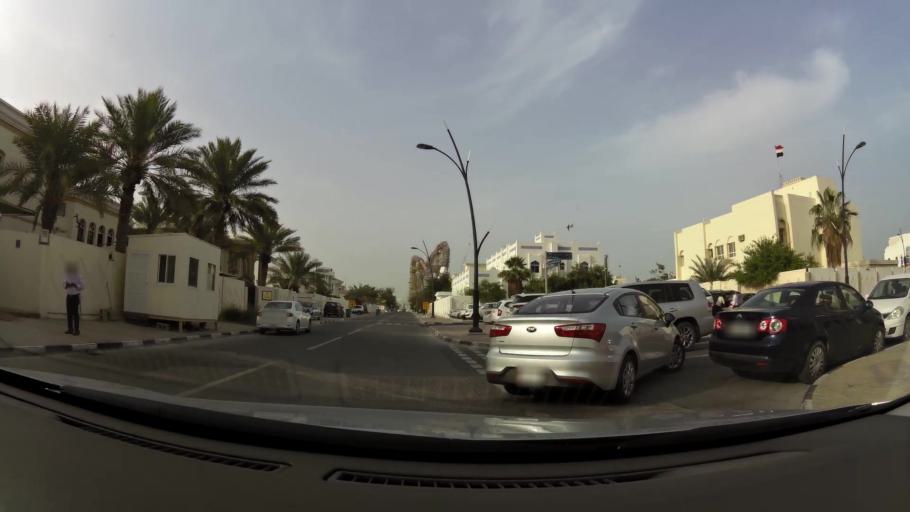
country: QA
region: Baladiyat ad Dawhah
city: Doha
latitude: 25.3297
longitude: 51.5176
